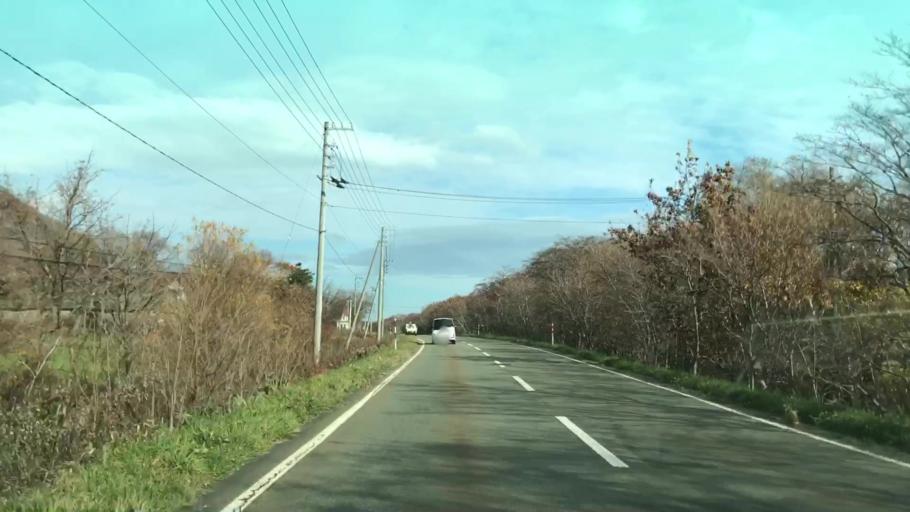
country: JP
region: Hokkaido
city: Obihiro
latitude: 42.0239
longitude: 143.2643
